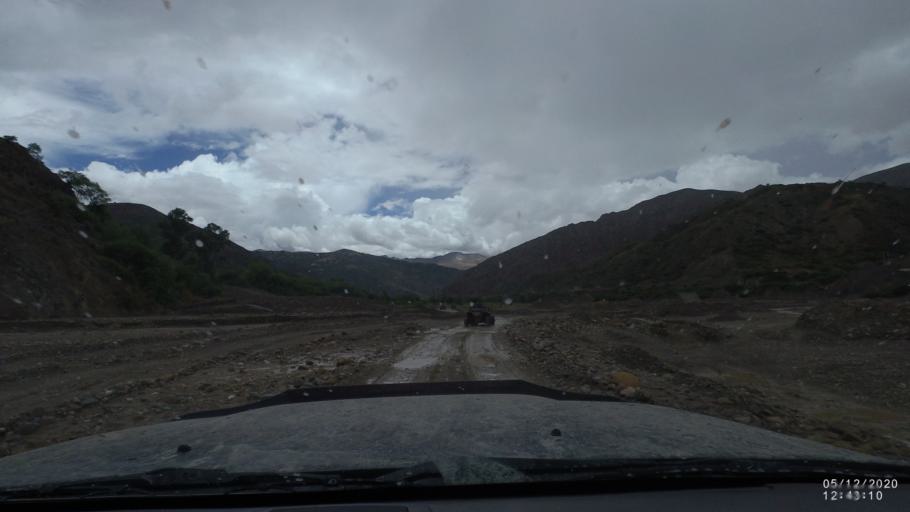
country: BO
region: Cochabamba
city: Sipe Sipe
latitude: -17.5490
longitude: -66.4357
